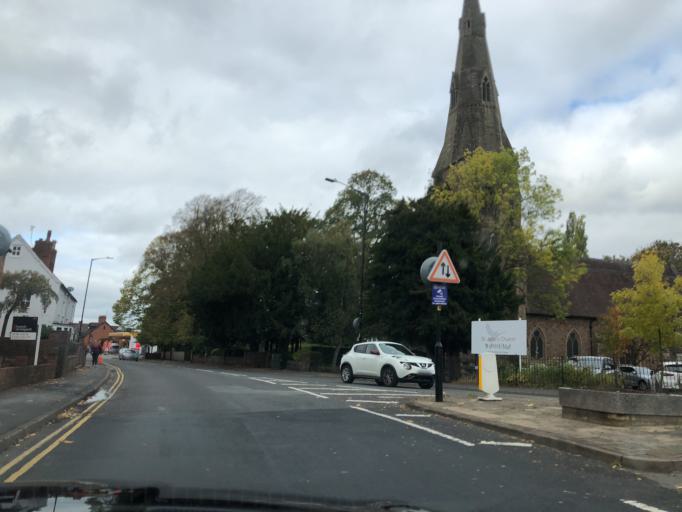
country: GB
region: England
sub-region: Warwickshire
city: Kenilworth
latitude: 52.3365
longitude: -1.5729
